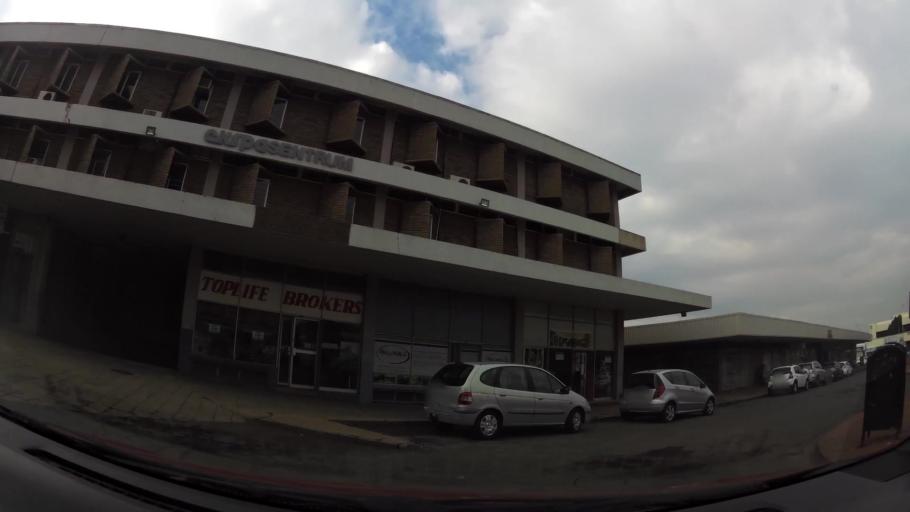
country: ZA
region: Gauteng
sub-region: Sedibeng District Municipality
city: Vanderbijlpark
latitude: -26.6995
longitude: 27.8370
